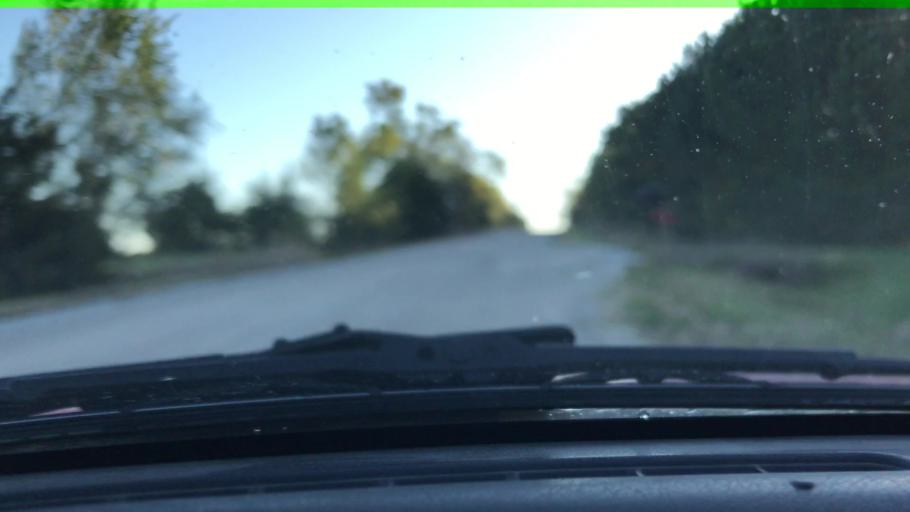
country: US
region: Nebraska
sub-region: Lancaster County
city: Lincoln
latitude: 40.7530
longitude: -96.7529
